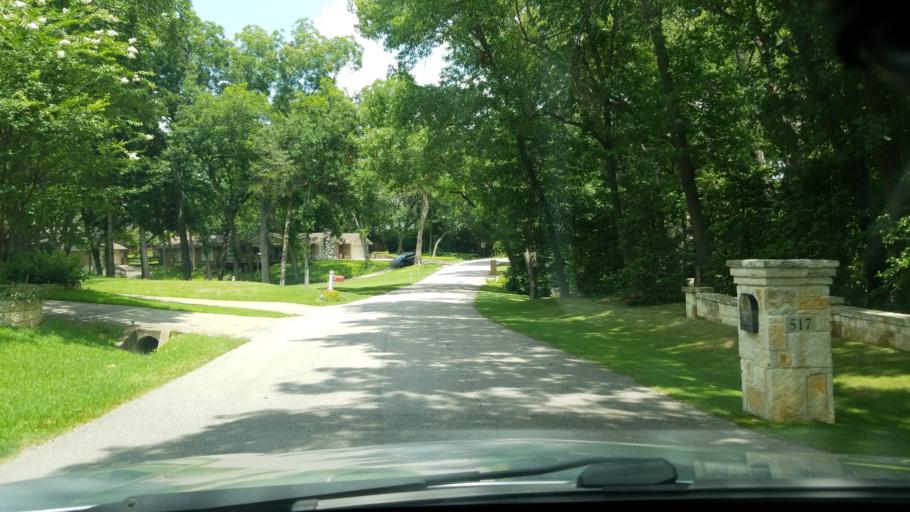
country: US
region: Texas
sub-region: Dallas County
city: Coppell
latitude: 32.9584
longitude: -96.9786
